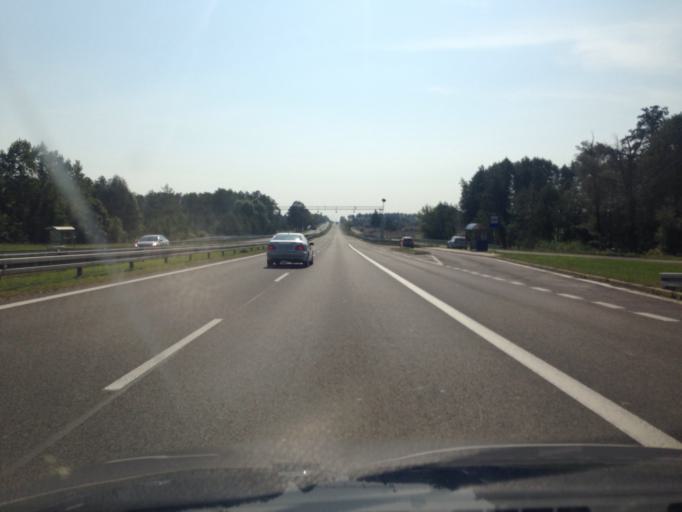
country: PL
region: Masovian Voivodeship
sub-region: Powiat plonski
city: Zaluski
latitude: 52.5676
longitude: 20.4872
